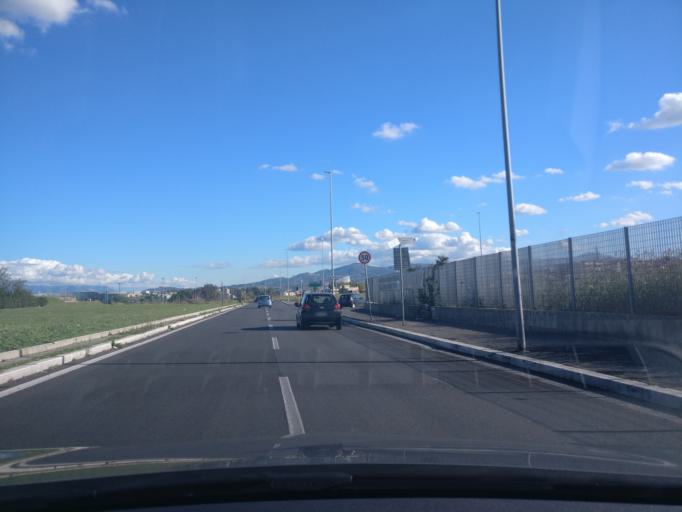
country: IT
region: Latium
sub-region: Citta metropolitana di Roma Capitale
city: Ciampino
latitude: 41.8546
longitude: 12.6078
